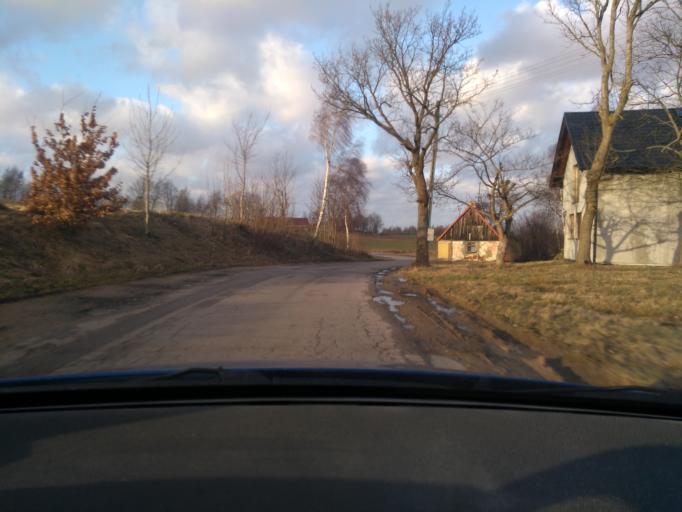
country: PL
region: Pomeranian Voivodeship
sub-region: Powiat kartuski
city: Kartuzy
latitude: 54.3854
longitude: 18.2206
